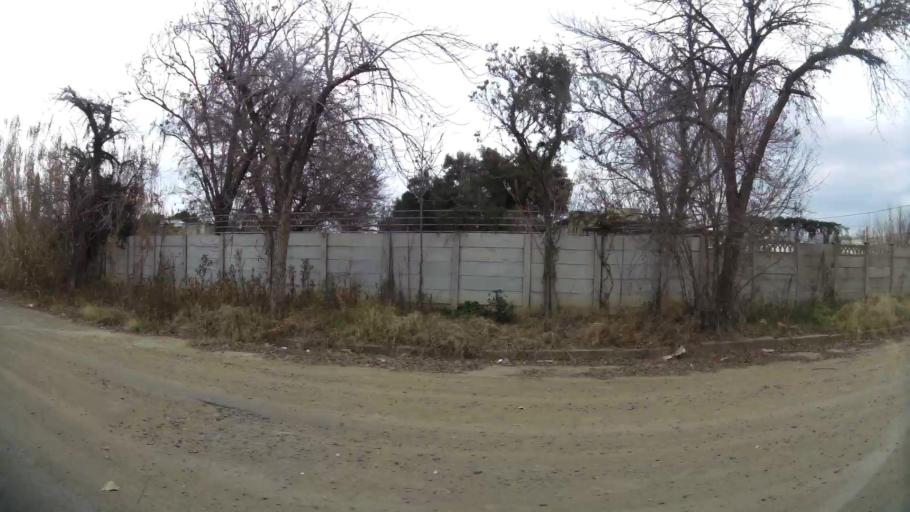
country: ZA
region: Orange Free State
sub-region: Fezile Dabi District Municipality
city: Kroonstad
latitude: -27.6733
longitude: 27.2303
